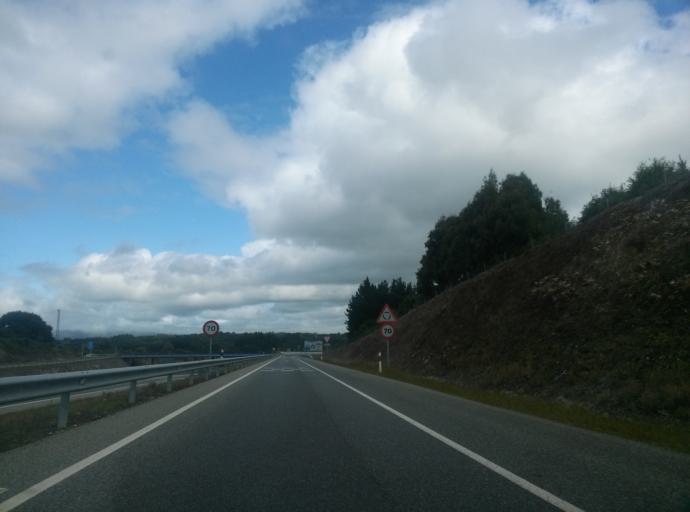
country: ES
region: Galicia
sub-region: Provincia de Lugo
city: Vilalba
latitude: 43.3169
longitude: -7.6975
